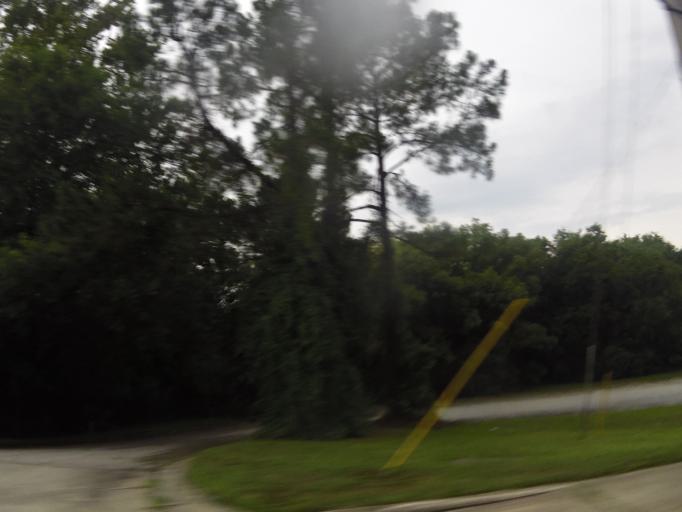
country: US
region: Florida
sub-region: Duval County
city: Jacksonville
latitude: 30.2742
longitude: -81.5604
